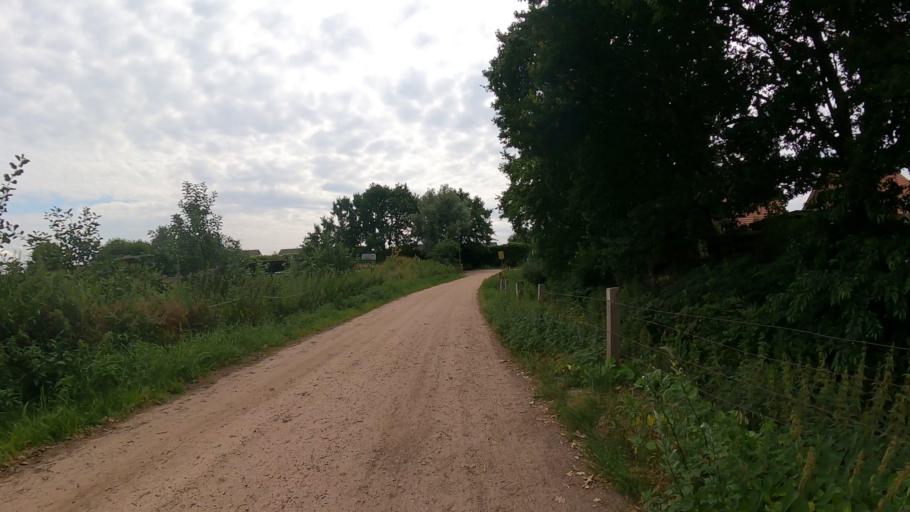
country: DE
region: Lower Saxony
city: Neu Wulmstorf
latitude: 53.4746
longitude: 9.7983
